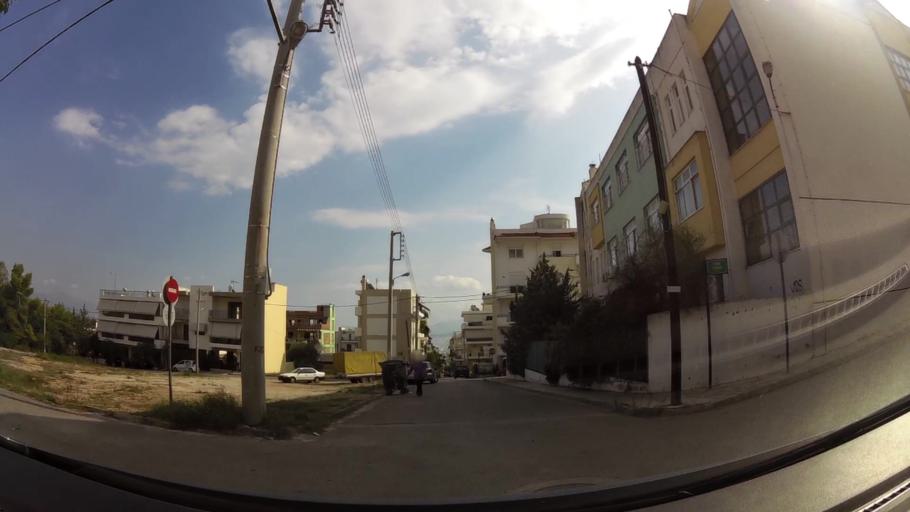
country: GR
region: Attica
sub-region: Nomarchia Athinas
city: Petroupolis
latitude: 38.0485
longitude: 23.6883
